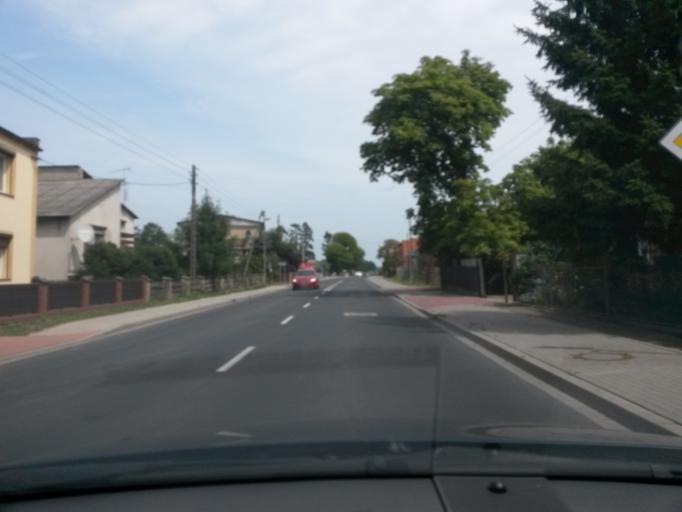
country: PL
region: Greater Poland Voivodeship
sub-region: Powiat sremski
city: Dolsk
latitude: 51.9506
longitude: 17.0596
